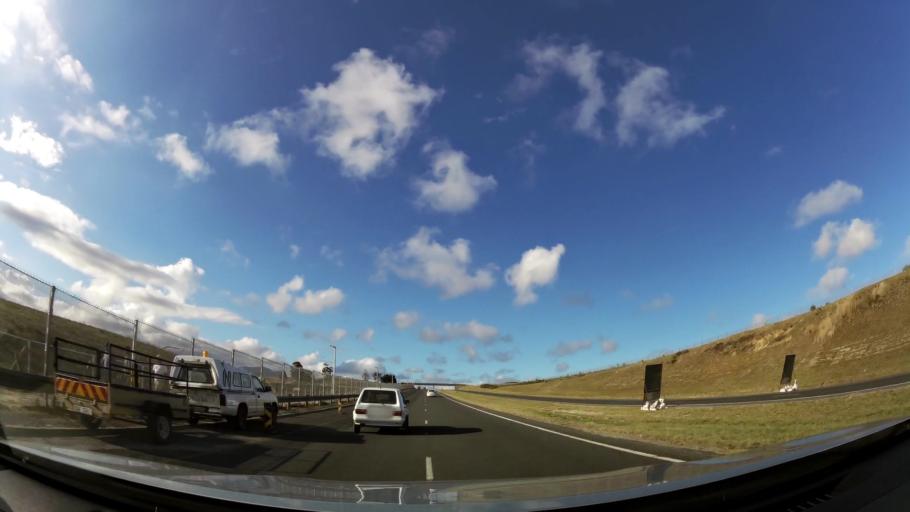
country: ZA
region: Western Cape
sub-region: Eden District Municipality
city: George
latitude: -33.9923
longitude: 22.4964
